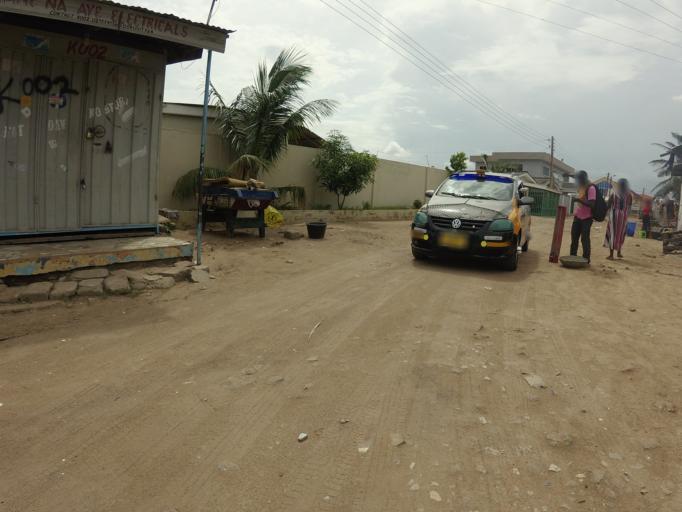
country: GH
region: Greater Accra
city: Accra
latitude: 5.5967
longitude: -0.2195
